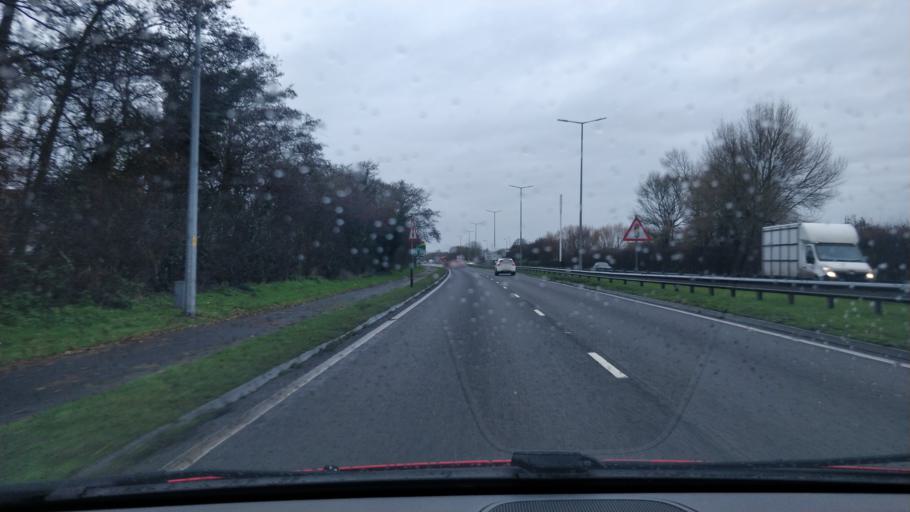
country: GB
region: England
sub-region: Sefton
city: Formby
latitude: 53.5517
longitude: -3.0462
